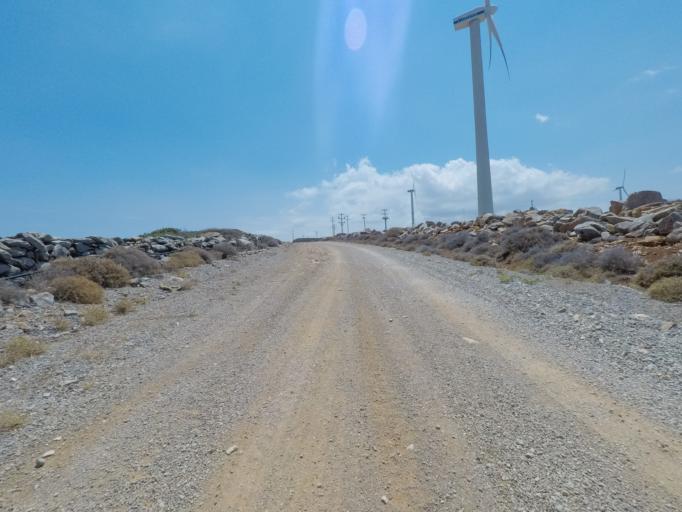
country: GR
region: Crete
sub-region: Nomos Lasithiou
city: Elounda
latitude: 35.3260
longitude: 25.7554
